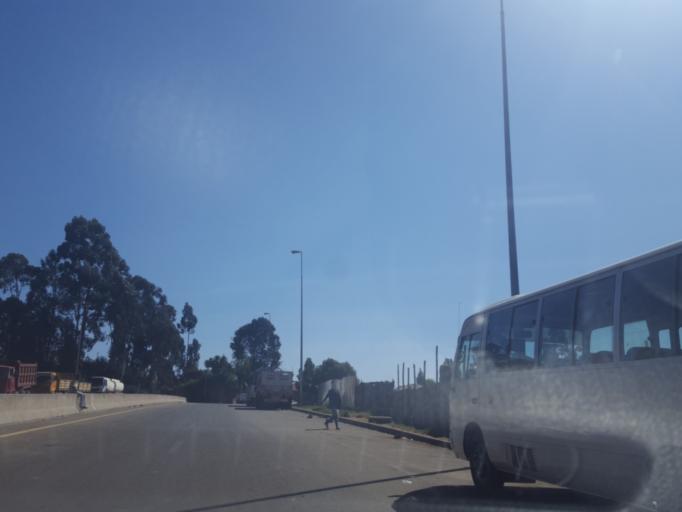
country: ET
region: Adis Abeba
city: Addis Ababa
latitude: 9.0628
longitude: 38.7374
